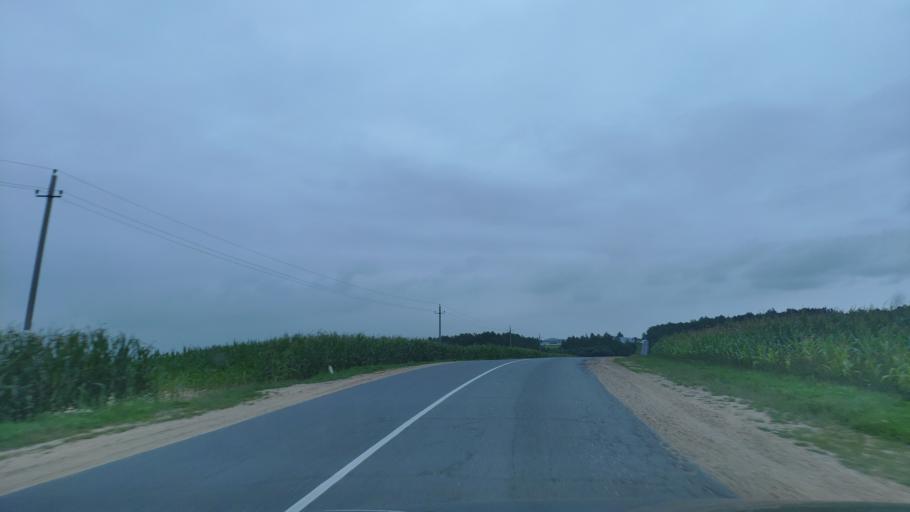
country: BY
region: Minsk
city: Azyartso
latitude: 53.8374
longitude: 27.3577
